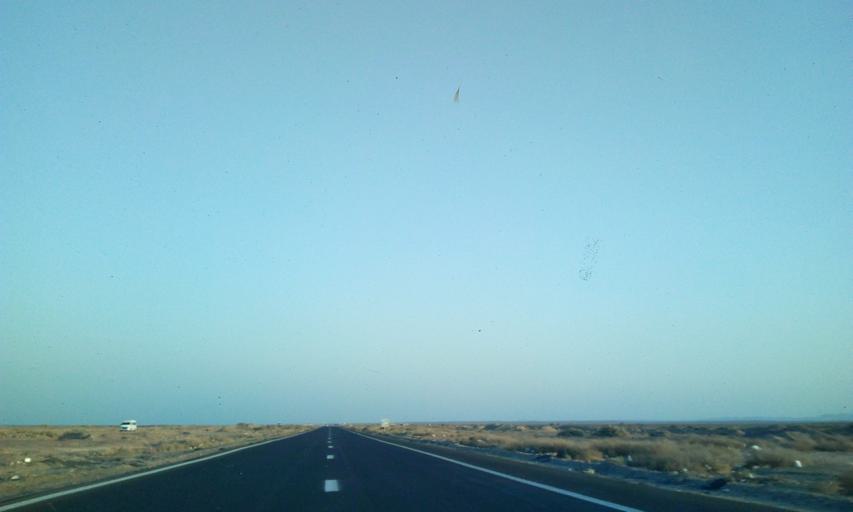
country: EG
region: South Sinai
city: Tor
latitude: 27.8525
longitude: 33.4336
